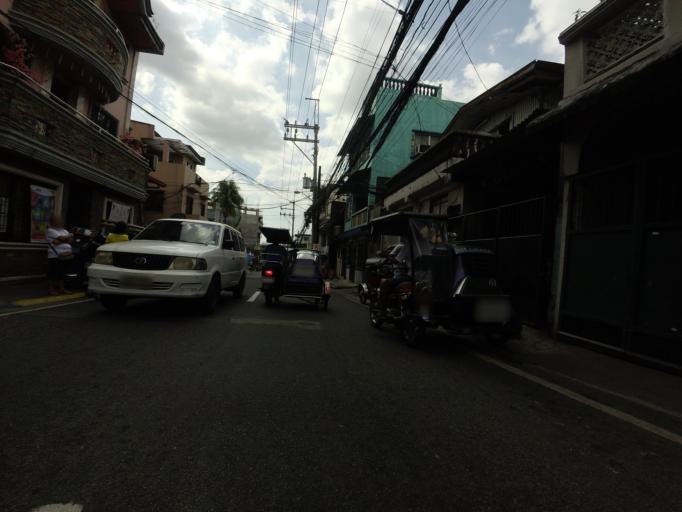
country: PH
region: Metro Manila
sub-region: San Juan
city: San Juan
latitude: 14.5890
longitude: 121.0274
